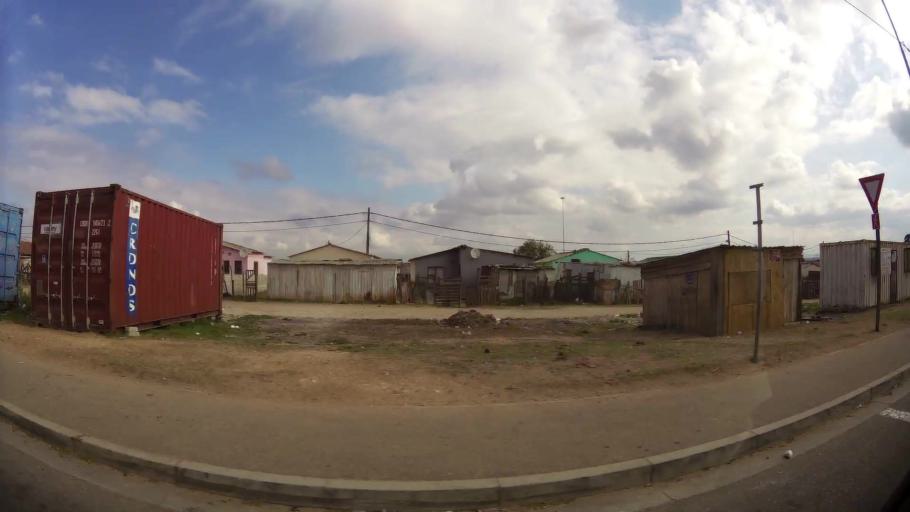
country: ZA
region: Eastern Cape
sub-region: Nelson Mandela Bay Metropolitan Municipality
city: Port Elizabeth
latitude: -33.7963
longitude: 25.5831
